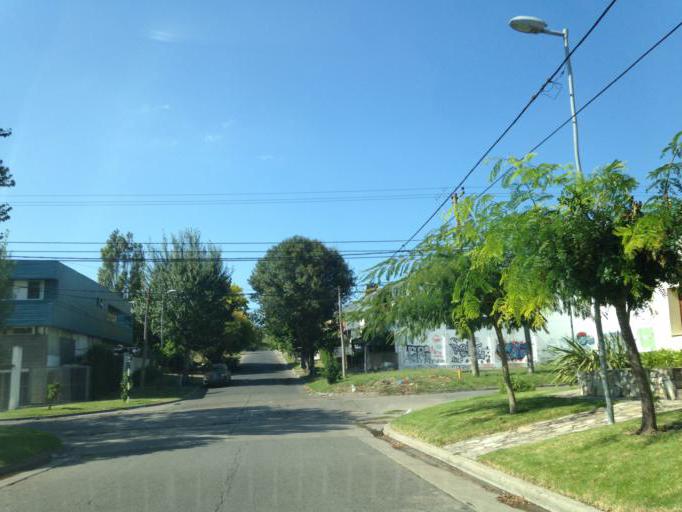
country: AR
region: Buenos Aires
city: Mar del Plata
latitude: -38.0320
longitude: -57.5478
